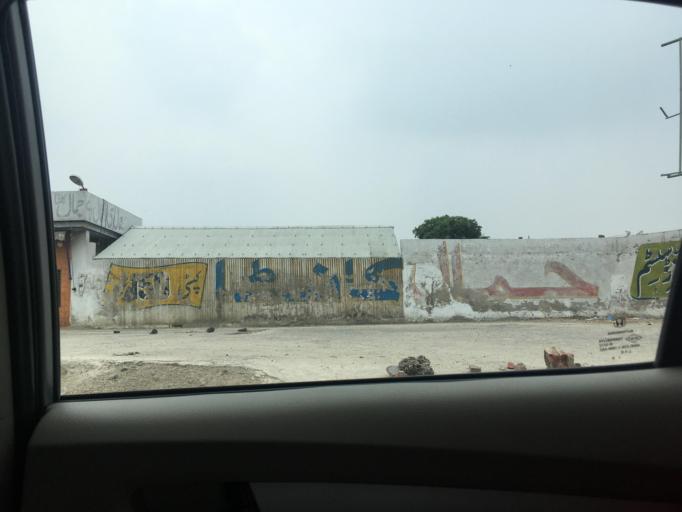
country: PK
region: Punjab
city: Lahore
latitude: 31.6090
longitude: 74.3533
